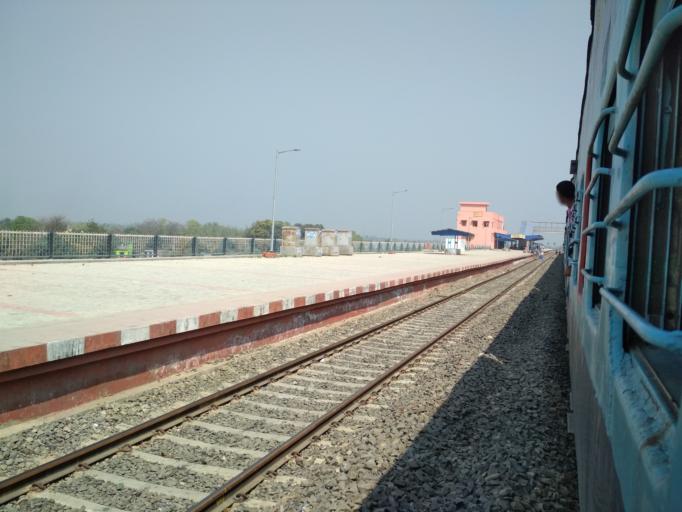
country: IN
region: Bihar
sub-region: Munger
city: Munger
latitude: 25.4262
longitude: 86.4386
